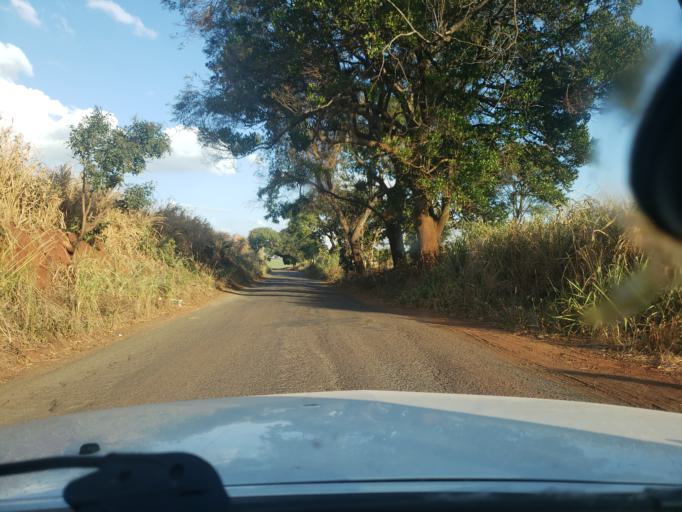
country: BR
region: Sao Paulo
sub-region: Mogi-Mirim
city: Mogi Mirim
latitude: -22.4651
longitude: -46.9332
